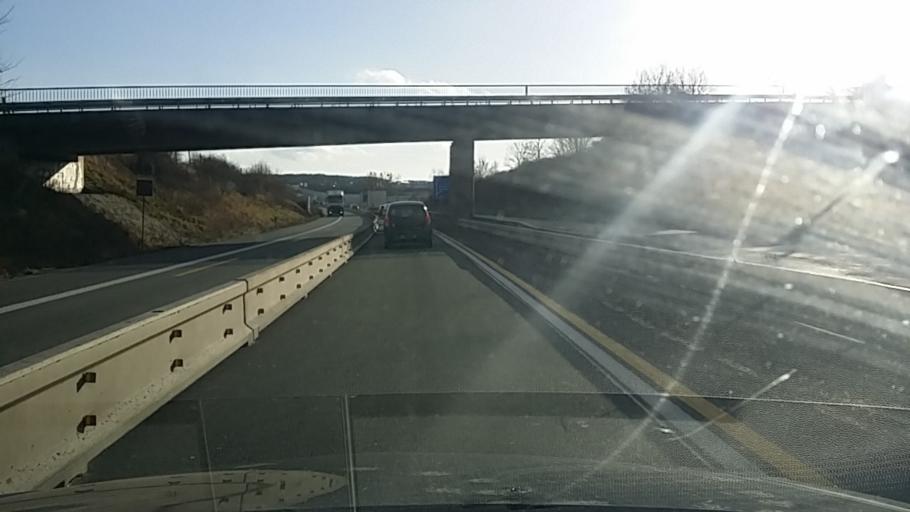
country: DE
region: North Rhine-Westphalia
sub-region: Regierungsbezirk Detmold
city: Paderborn
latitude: 51.6588
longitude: 8.7085
